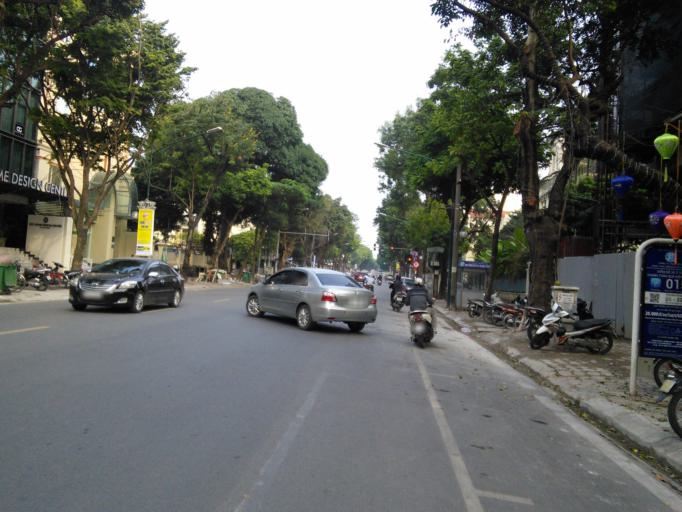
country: VN
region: Ha Noi
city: Hoan Kiem
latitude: 21.0222
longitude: 105.8478
